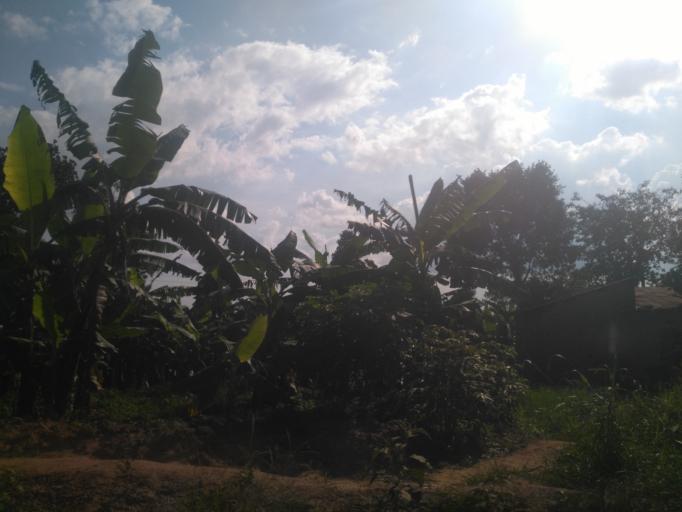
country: UG
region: Central Region
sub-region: Wakiso District
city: Wakiso
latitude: 0.2968
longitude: 32.4512
